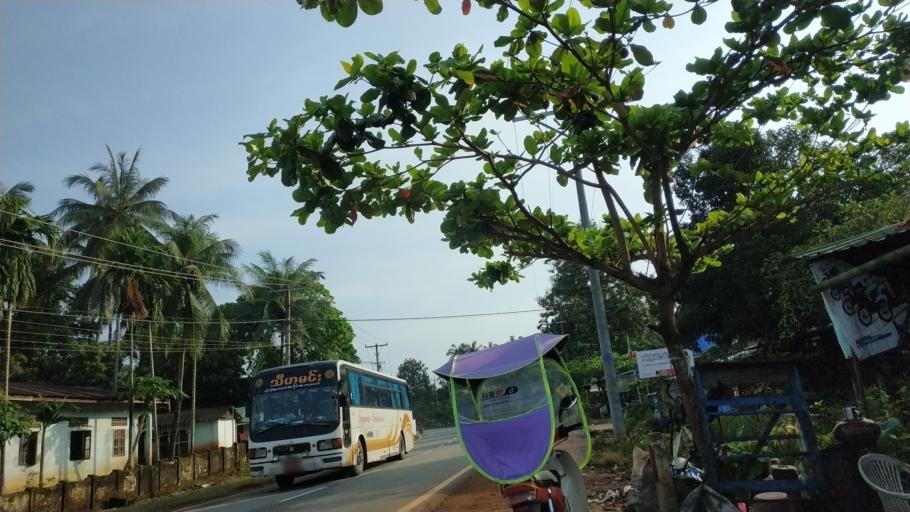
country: MM
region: Tanintharyi
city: Dawei
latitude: 14.2486
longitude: 98.2041
